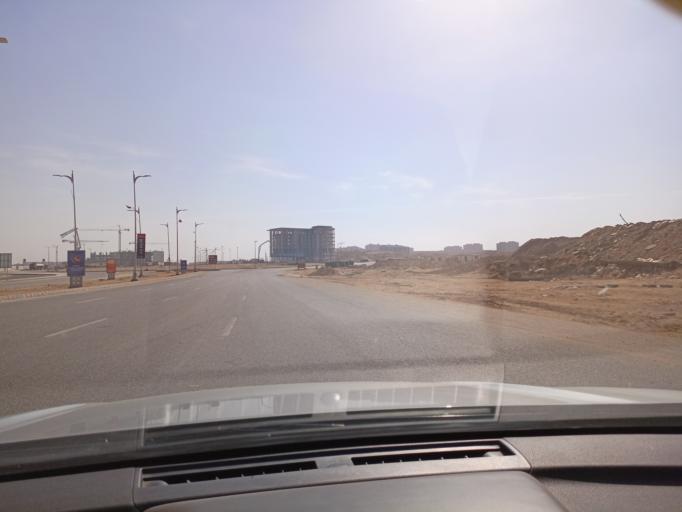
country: EG
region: Muhafazat al Qalyubiyah
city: Al Khankah
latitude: 30.0402
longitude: 31.6849
